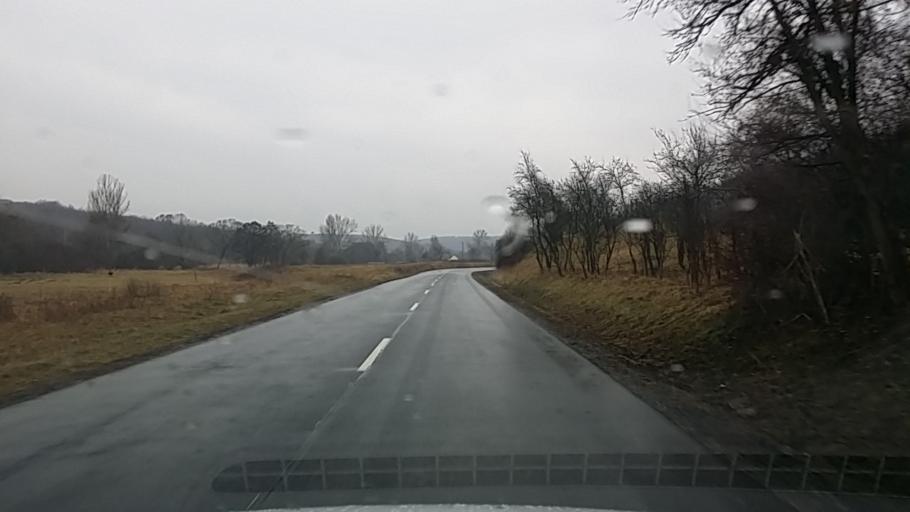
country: HU
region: Borsod-Abauj-Zemplen
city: Rudabanya
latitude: 48.4158
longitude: 20.5054
